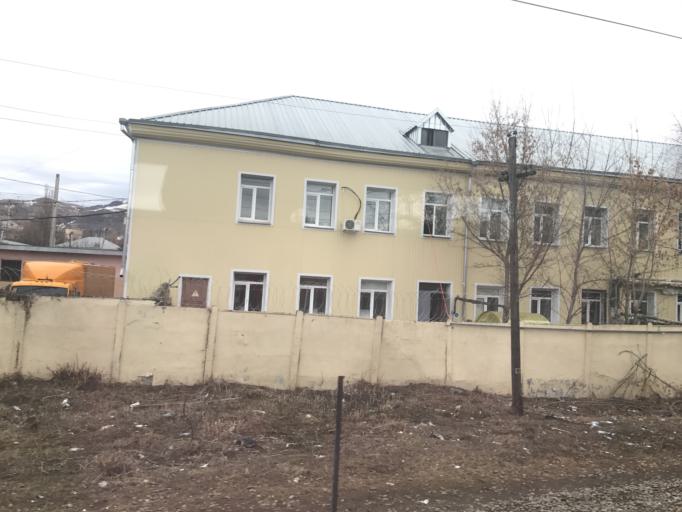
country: RU
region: Stavropol'skiy
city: Kislovodsk
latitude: 43.9250
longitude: 42.7251
